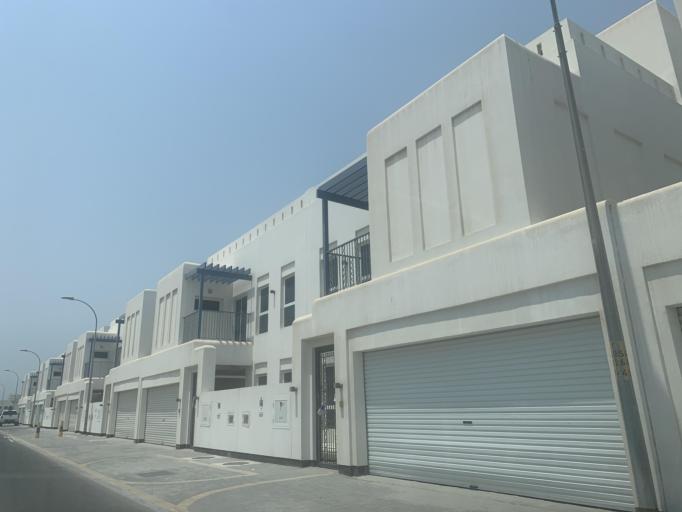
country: BH
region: Muharraq
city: Al Muharraq
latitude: 26.3127
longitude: 50.6243
